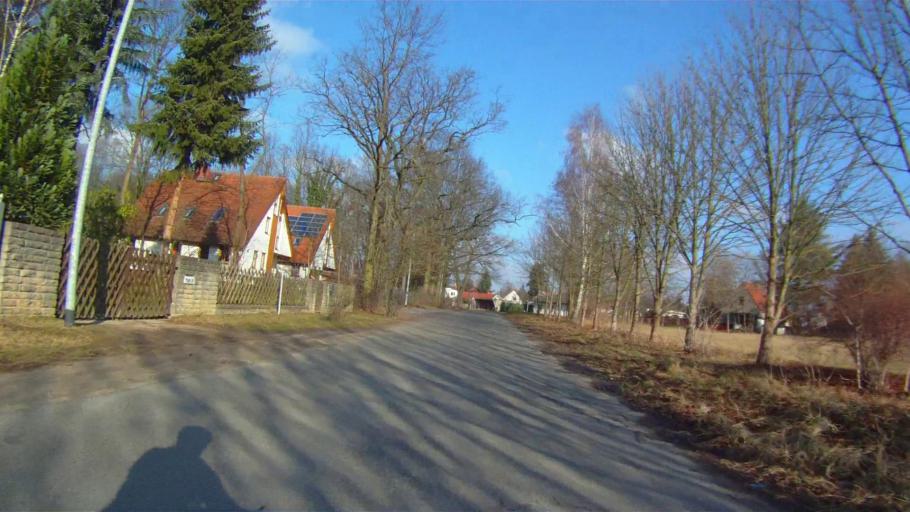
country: DE
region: Brandenburg
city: Schoneiche
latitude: 52.4715
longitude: 13.7156
